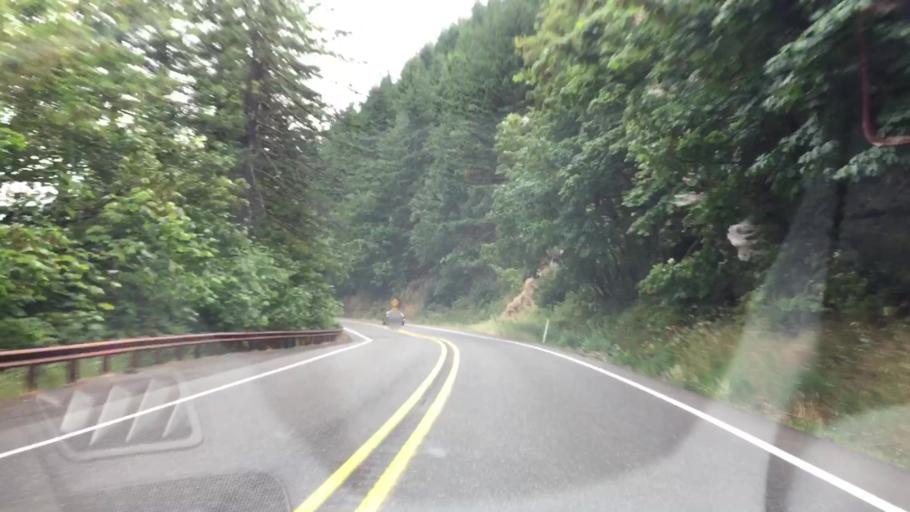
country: US
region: Washington
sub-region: Clark County
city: Washougal
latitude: 45.5824
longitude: -122.1947
